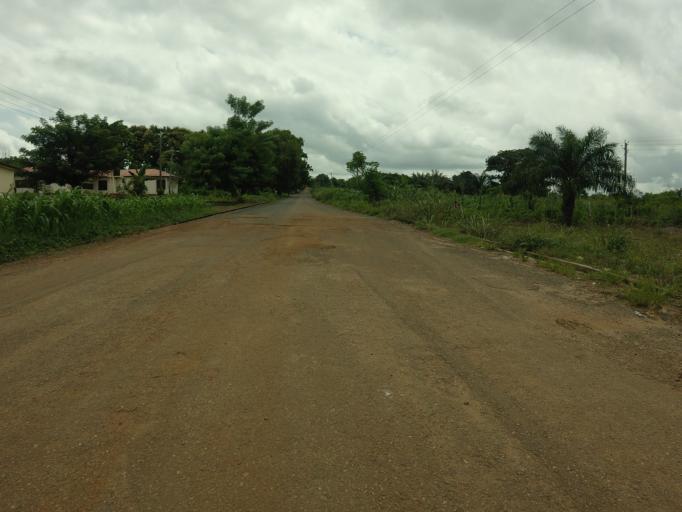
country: GH
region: Volta
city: Ho
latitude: 6.5949
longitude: 0.4596
